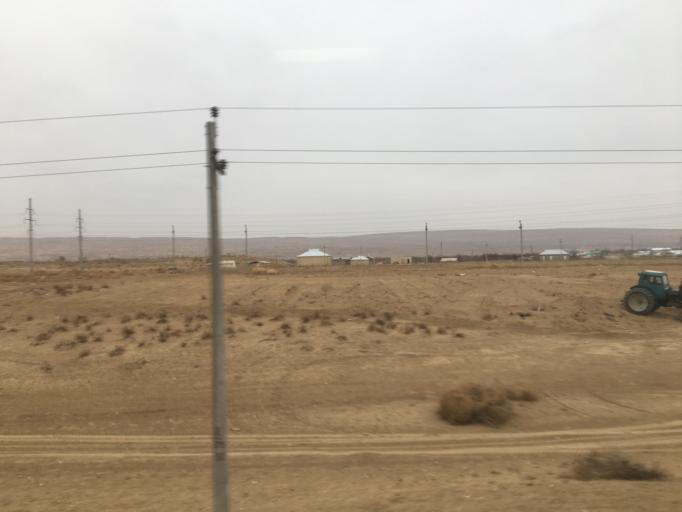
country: TM
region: Mary
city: Yoloeten
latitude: 36.5498
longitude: 62.5525
